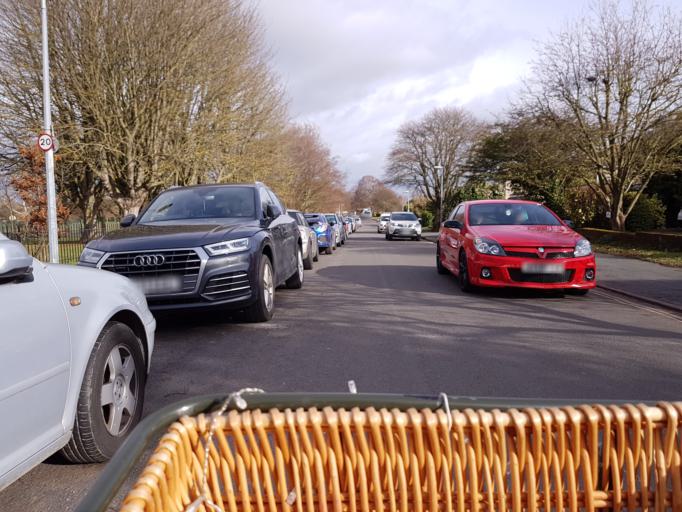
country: GB
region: England
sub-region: Cambridgeshire
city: Cambridge
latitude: 52.1760
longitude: 0.1488
